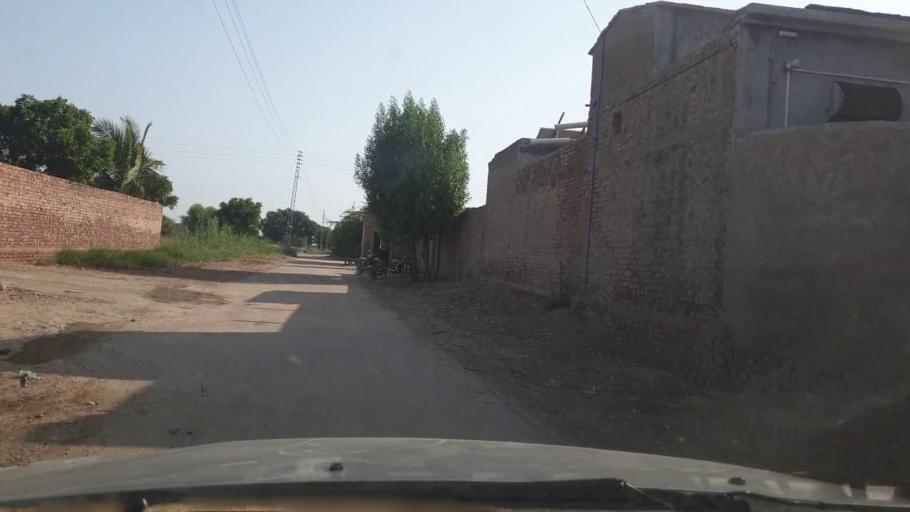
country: PK
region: Sindh
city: Tando Ghulam Ali
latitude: 25.2088
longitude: 68.9640
